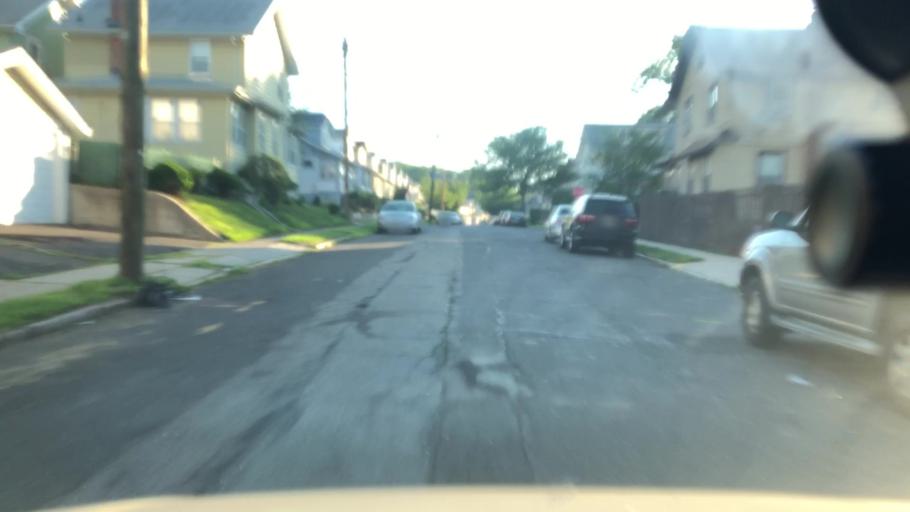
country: US
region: New Jersey
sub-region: Union County
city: Union
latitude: 40.7122
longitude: -74.2611
